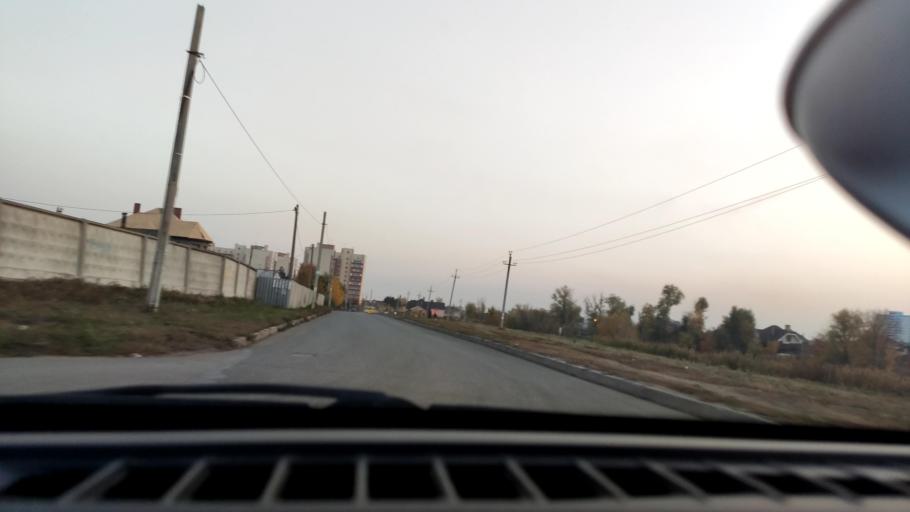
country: RU
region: Samara
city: Samara
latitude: 53.1540
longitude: 50.0880
